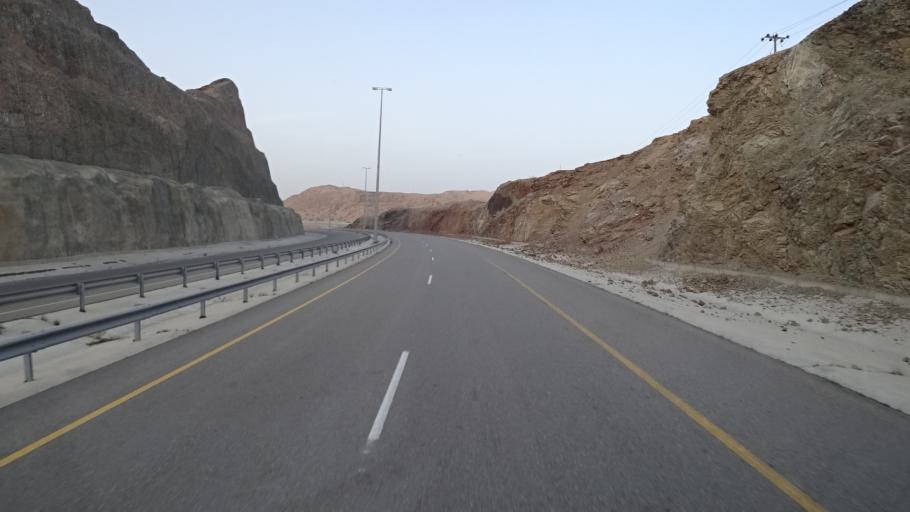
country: OM
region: Muhafazat Masqat
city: Muscat
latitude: 23.1925
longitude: 58.8775
